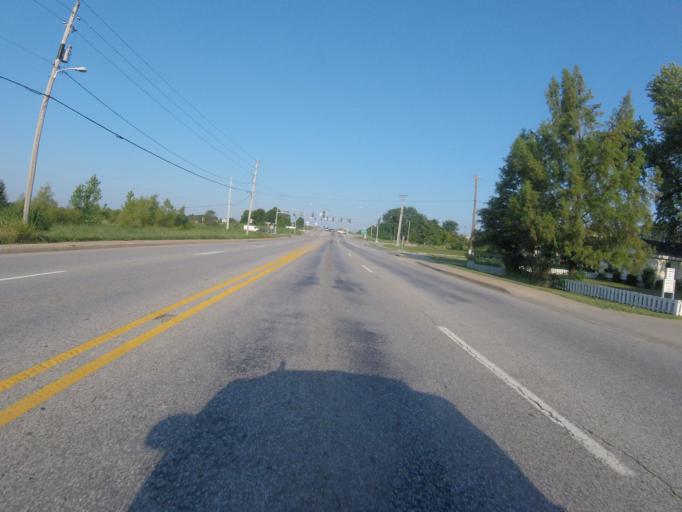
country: US
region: Arkansas
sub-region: Washington County
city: Fayetteville
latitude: 36.0782
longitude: -94.1972
